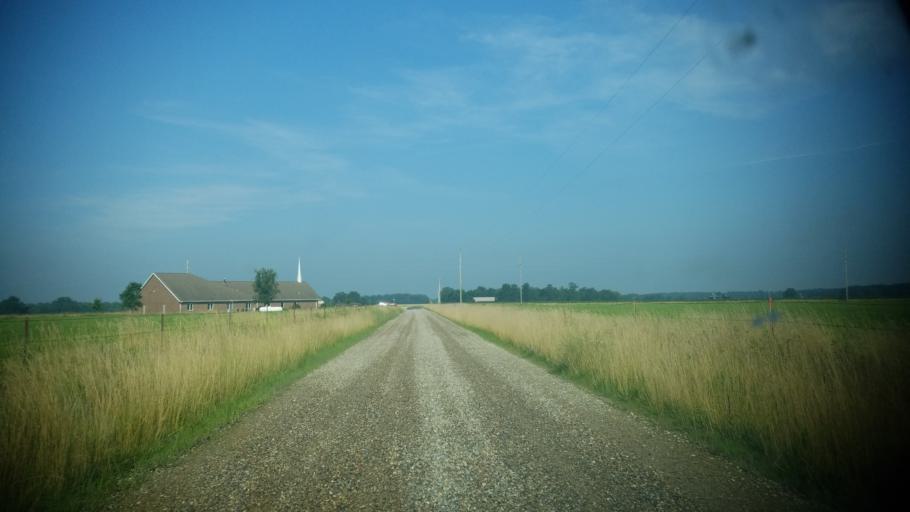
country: US
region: Illinois
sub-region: Clay County
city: Flora
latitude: 38.6024
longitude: -88.3803
